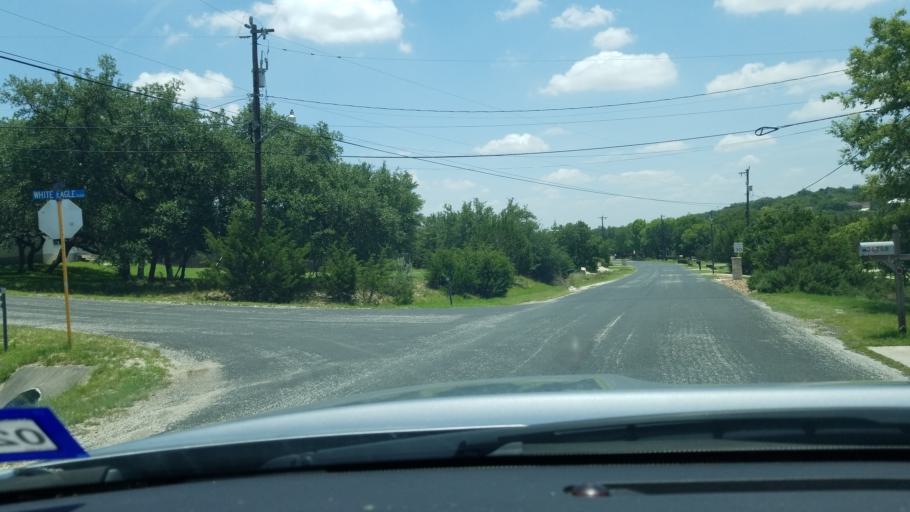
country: US
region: Texas
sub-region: Bexar County
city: Timberwood Park
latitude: 29.6887
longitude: -98.5004
